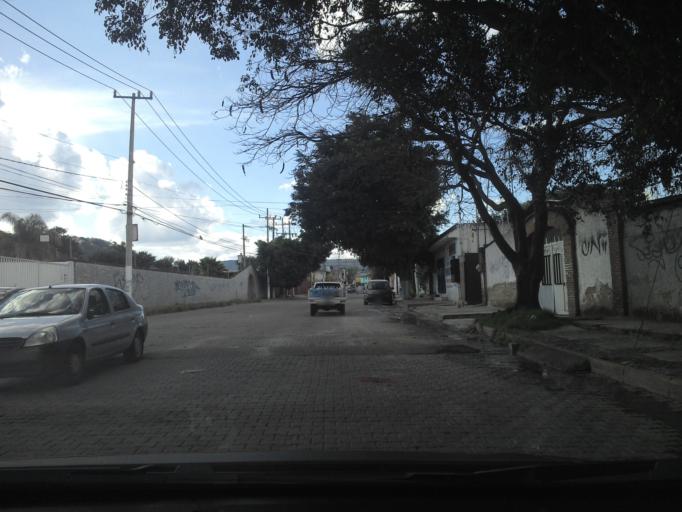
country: MX
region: Jalisco
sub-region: Tlajomulco de Zuniga
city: Palomar
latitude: 20.6180
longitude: -103.4517
